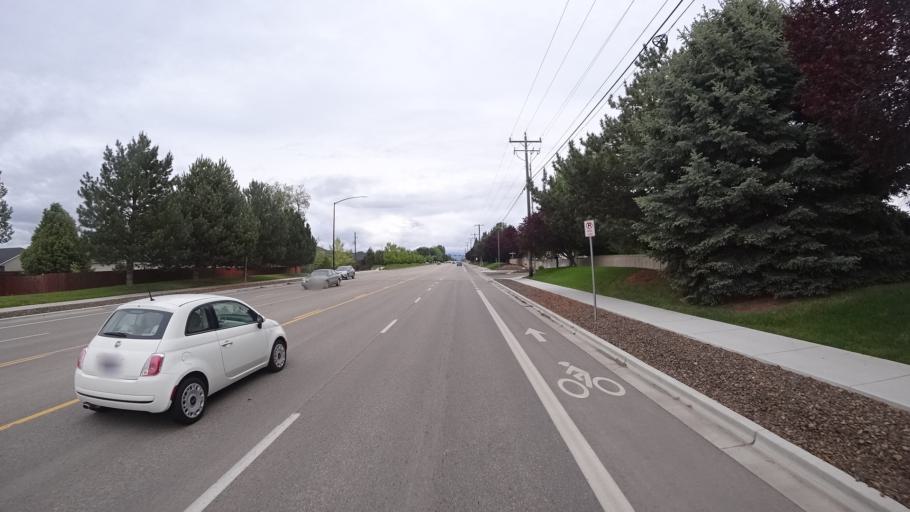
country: US
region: Idaho
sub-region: Ada County
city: Meridian
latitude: 43.6338
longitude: -116.3781
